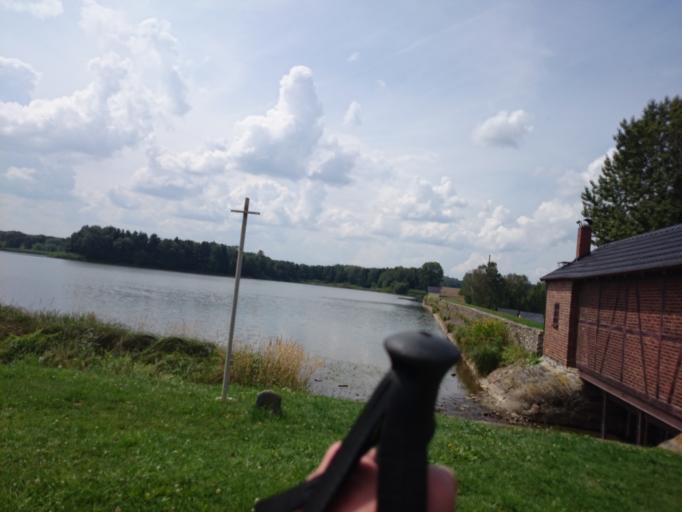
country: DE
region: Saxony
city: Freiberg
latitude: 50.8781
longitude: 13.3612
